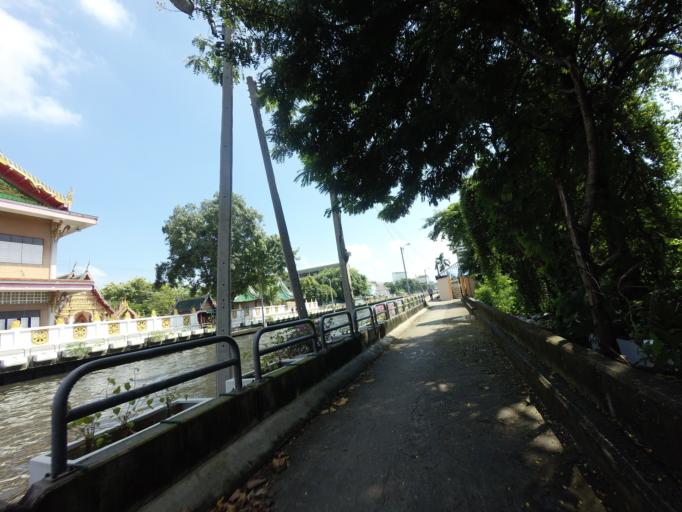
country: TH
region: Bangkok
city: Bang Kapi
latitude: 13.7635
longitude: 100.6358
